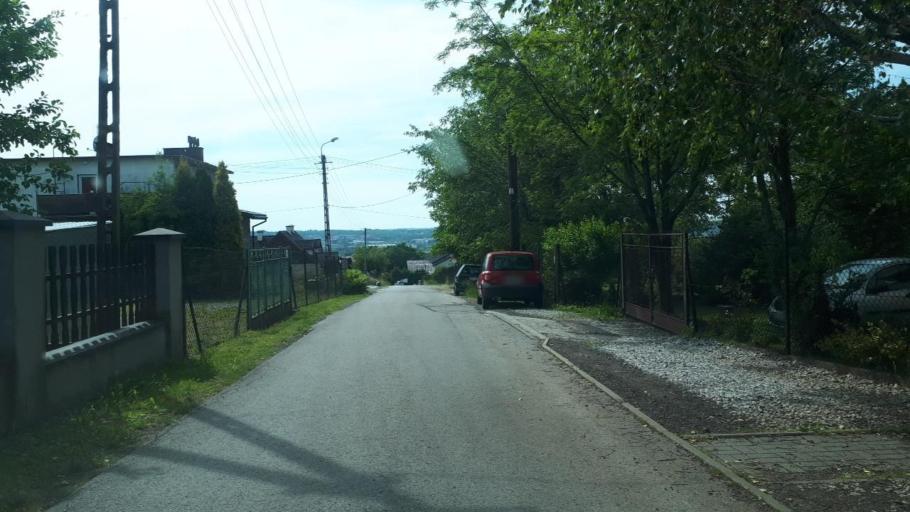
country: PL
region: Silesian Voivodeship
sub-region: Bielsko-Biala
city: Bielsko-Biala
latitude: 49.8462
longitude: 19.0788
